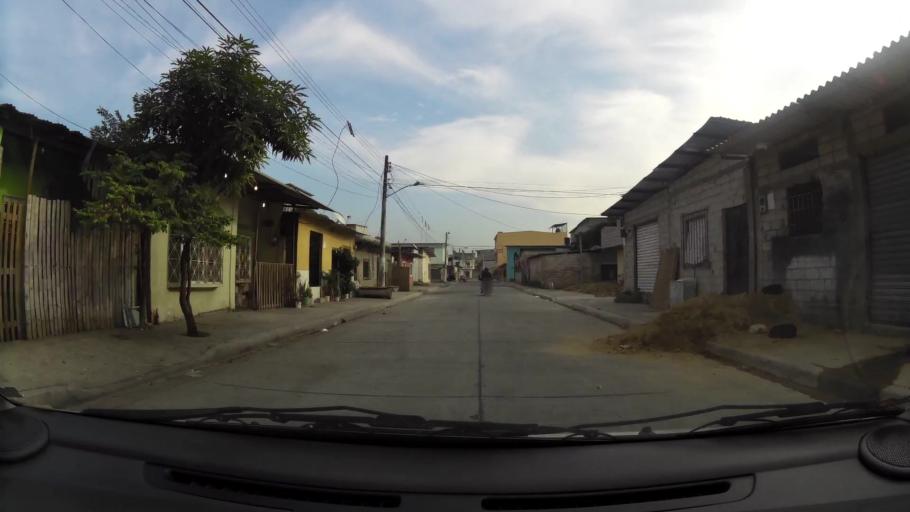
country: EC
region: Guayas
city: Eloy Alfaro
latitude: -2.0897
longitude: -79.9048
